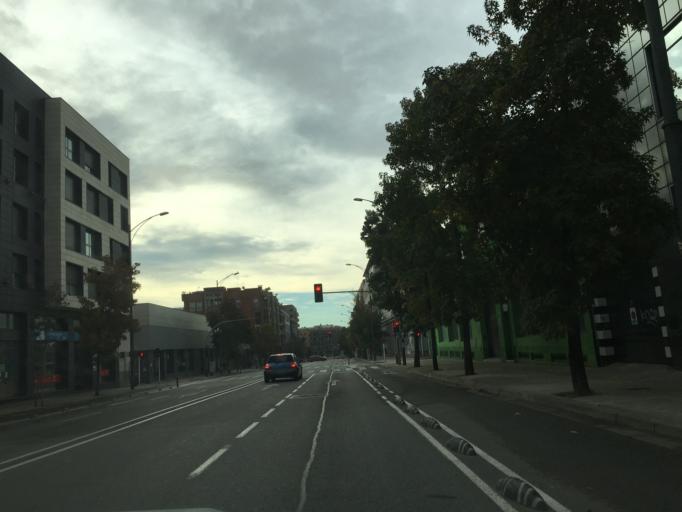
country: ES
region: Catalonia
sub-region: Provincia de Barcelona
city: Sabadell
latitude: 41.5474
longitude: 2.0991
